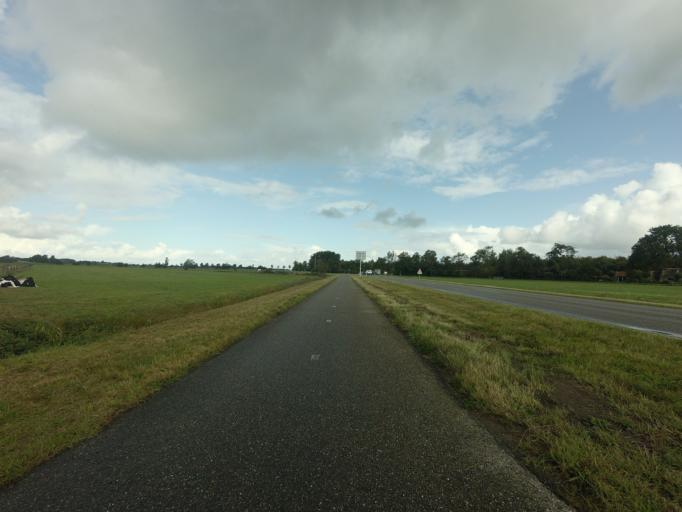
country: NL
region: Friesland
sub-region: Gemeente Tytsjerksteradiel
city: Garyp
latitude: 53.1589
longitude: 5.9503
